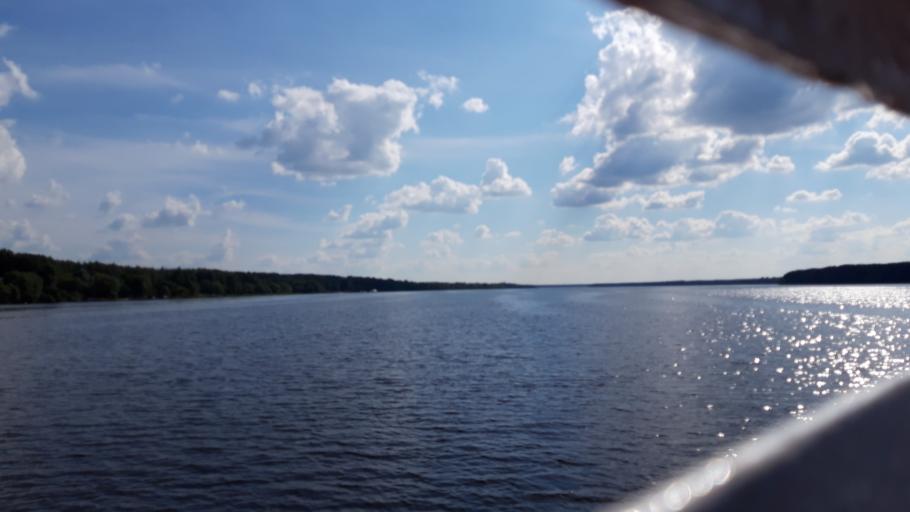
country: RU
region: Tverskaya
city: Konakovo
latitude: 56.6631
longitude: 36.6515
